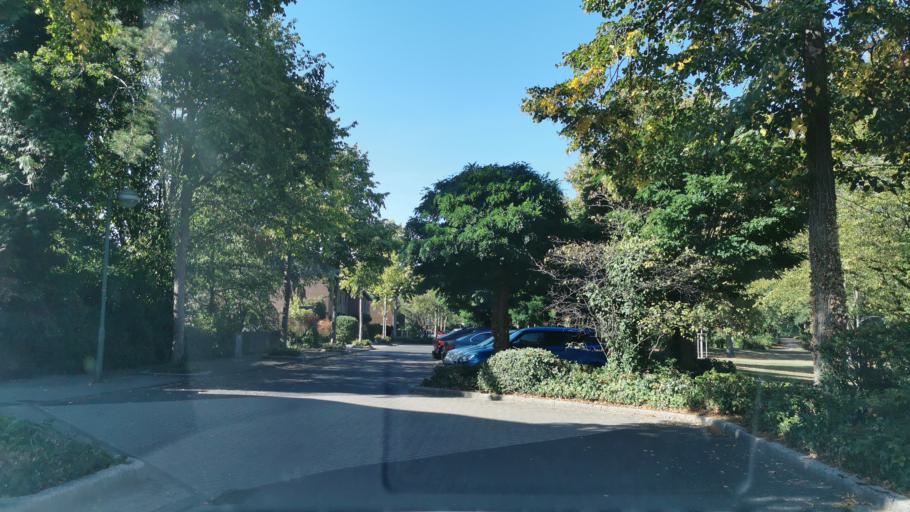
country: DE
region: North Rhine-Westphalia
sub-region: Regierungsbezirk Dusseldorf
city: Meerbusch
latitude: 51.2532
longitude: 6.6892
